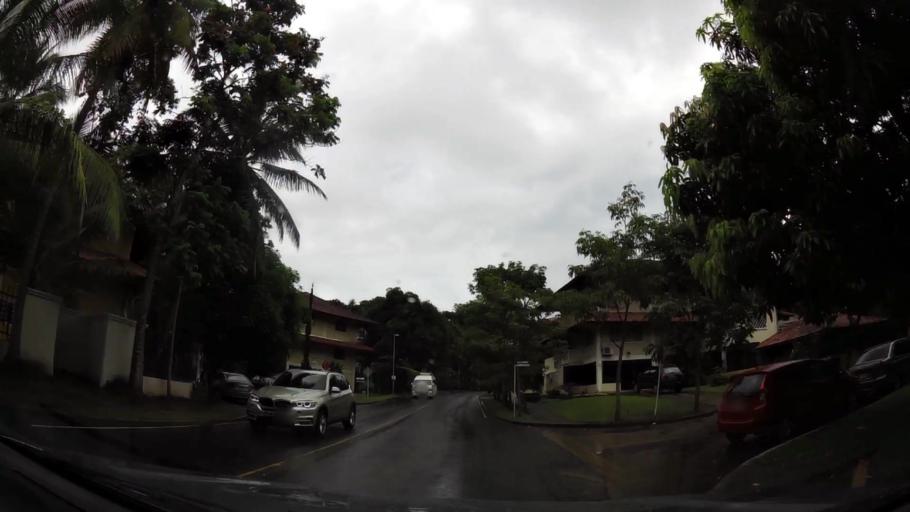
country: PA
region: Panama
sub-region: Distrito de Panama
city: Ancon
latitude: 8.9835
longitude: -79.5581
